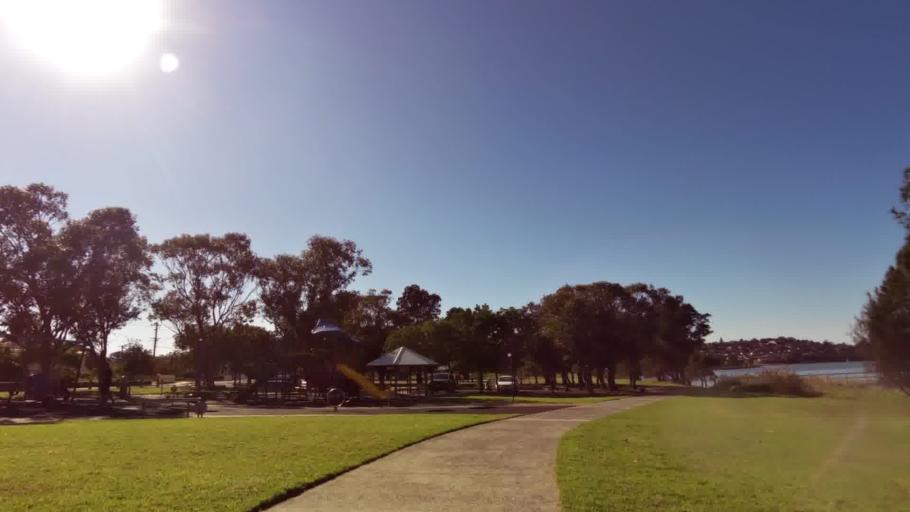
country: AU
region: New South Wales
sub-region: Wollongong
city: Berkeley
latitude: -34.4846
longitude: 150.8451
